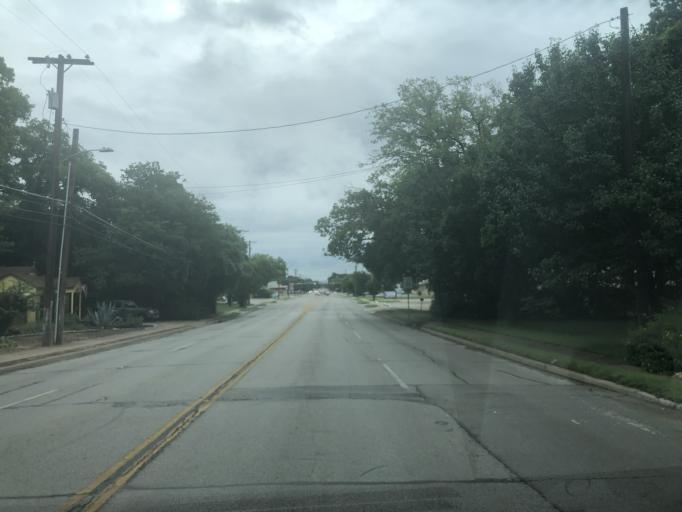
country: US
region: Texas
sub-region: Dallas County
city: Irving
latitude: 32.8010
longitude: -96.9378
